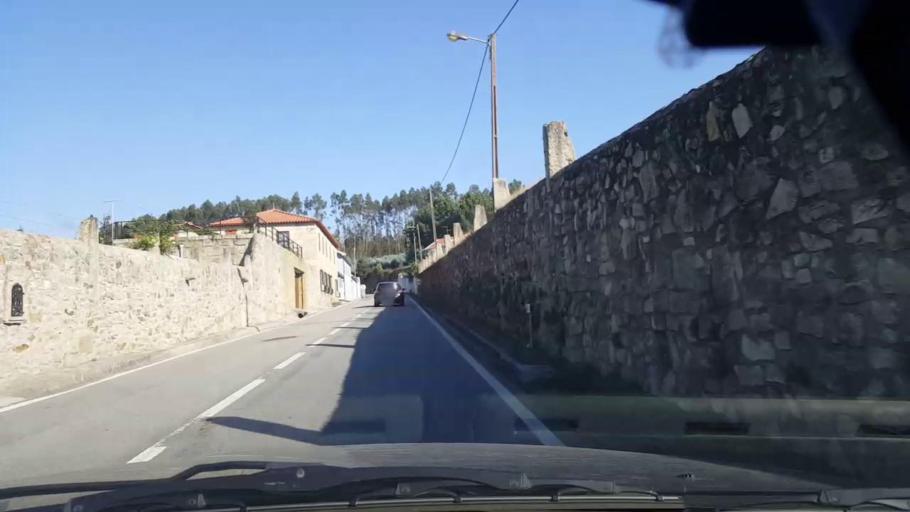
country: PT
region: Porto
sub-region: Maia
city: Gemunde
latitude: 41.3258
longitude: -8.6539
